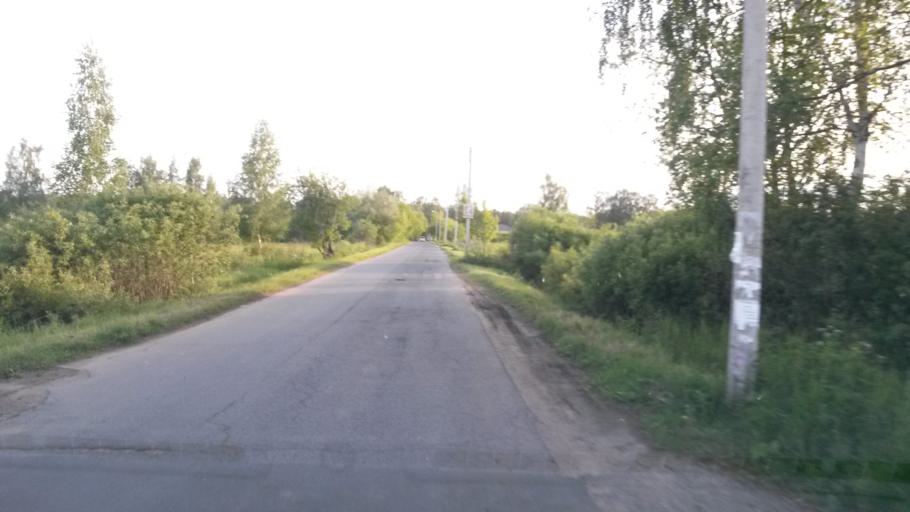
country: RU
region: Jaroslavl
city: Yaroslavl
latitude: 57.7035
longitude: 39.8304
